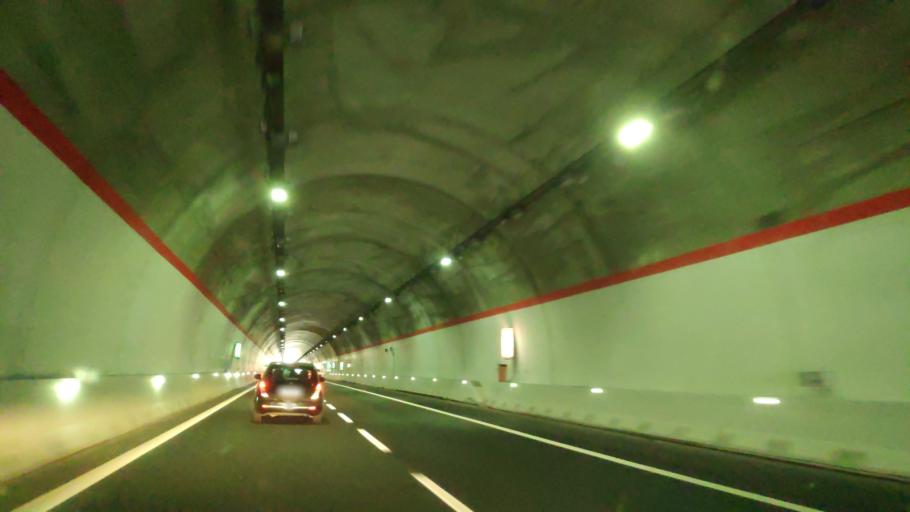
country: IT
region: Basilicate
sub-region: Provincia di Potenza
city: Lagonegro
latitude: 40.1621
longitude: 15.7336
